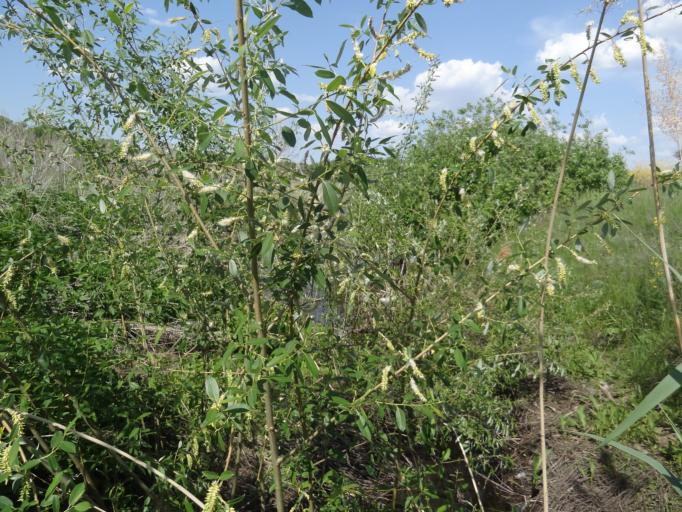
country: RU
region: Saratov
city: Privolzhskiy
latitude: 51.3610
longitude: 46.1299
